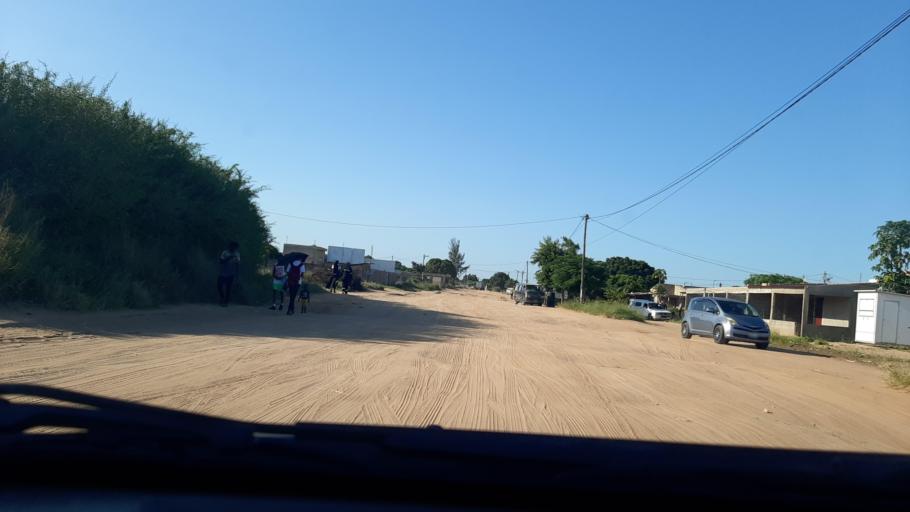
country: MZ
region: Maputo City
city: Maputo
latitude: -25.8064
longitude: 32.5467
